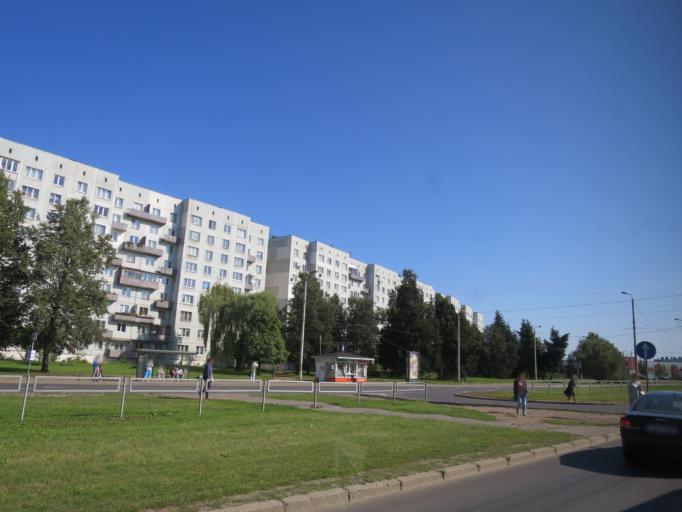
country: LV
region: Riga
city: Riga
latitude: 56.9588
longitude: 24.1803
